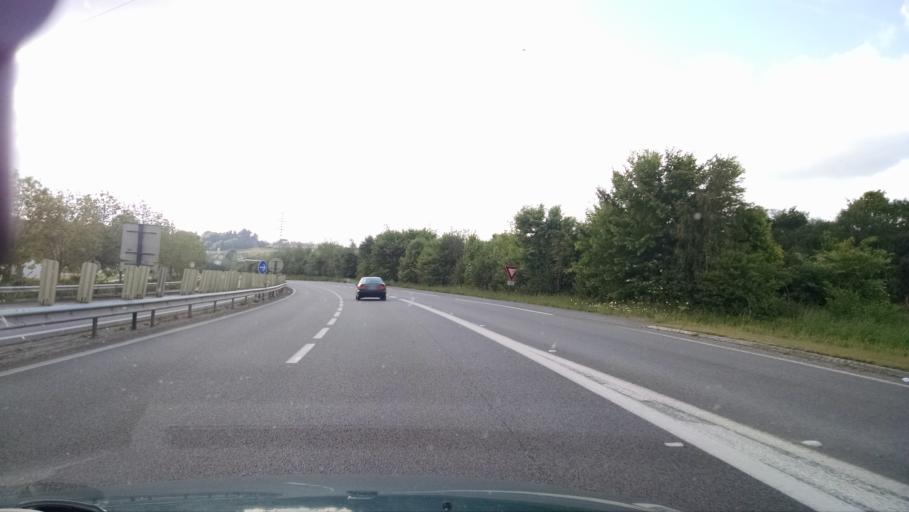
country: FR
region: Brittany
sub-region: Departement du Finistere
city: Morlaix
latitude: 48.5811
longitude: -3.8648
